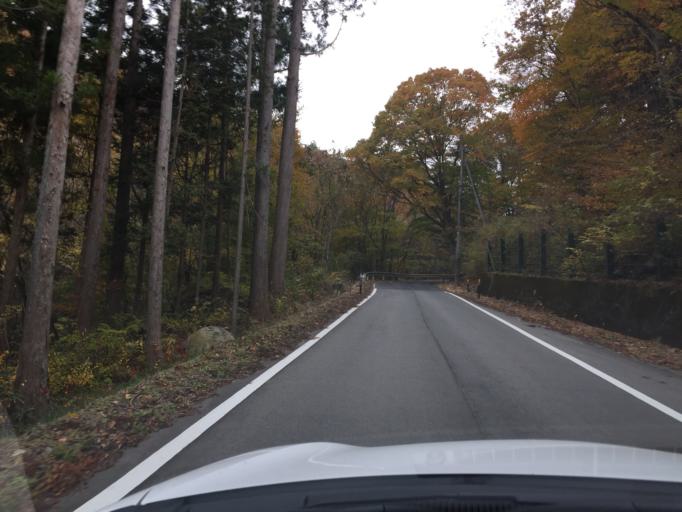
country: JP
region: Fukushima
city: Iwaki
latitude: 37.2044
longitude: 140.6978
